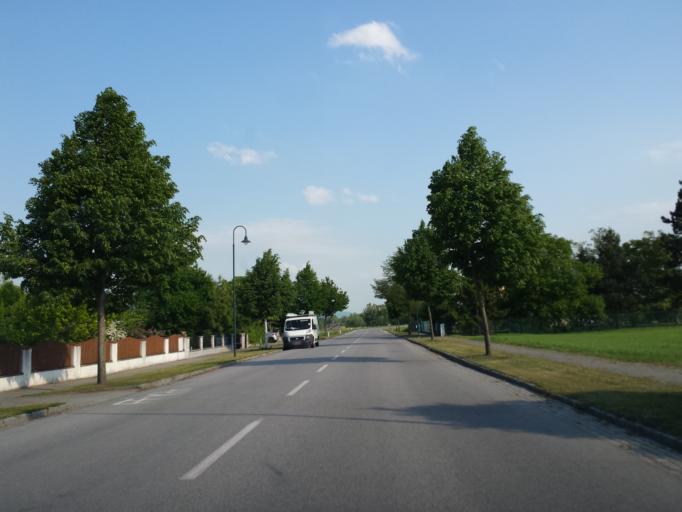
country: AT
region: Lower Austria
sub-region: Politischer Bezirk Ganserndorf
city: Marchegg
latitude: 48.3045
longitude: 16.8738
